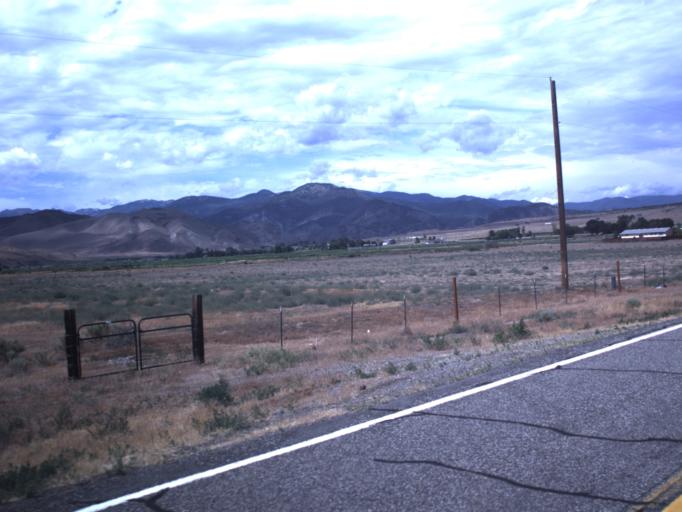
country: US
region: Utah
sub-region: Sevier County
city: Monroe
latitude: 38.6244
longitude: -112.2073
